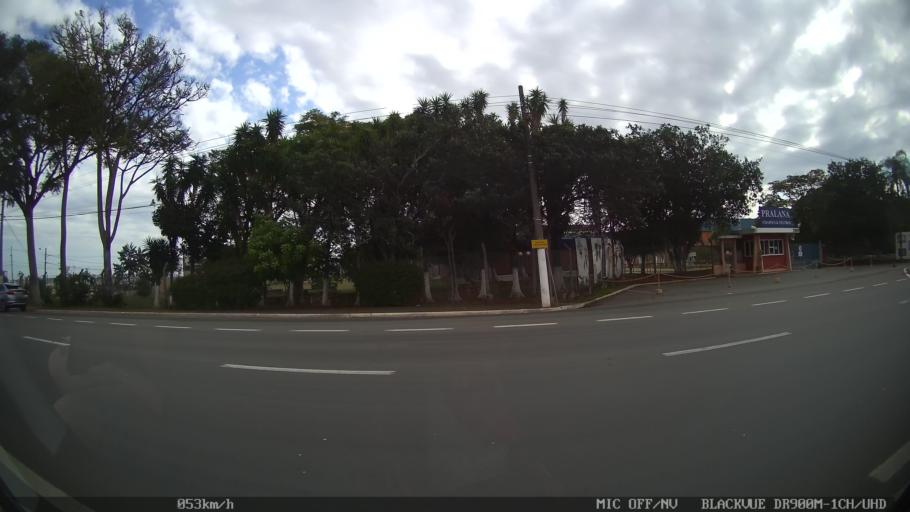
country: BR
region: Sao Paulo
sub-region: Limeira
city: Limeira
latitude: -22.5480
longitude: -47.3790
